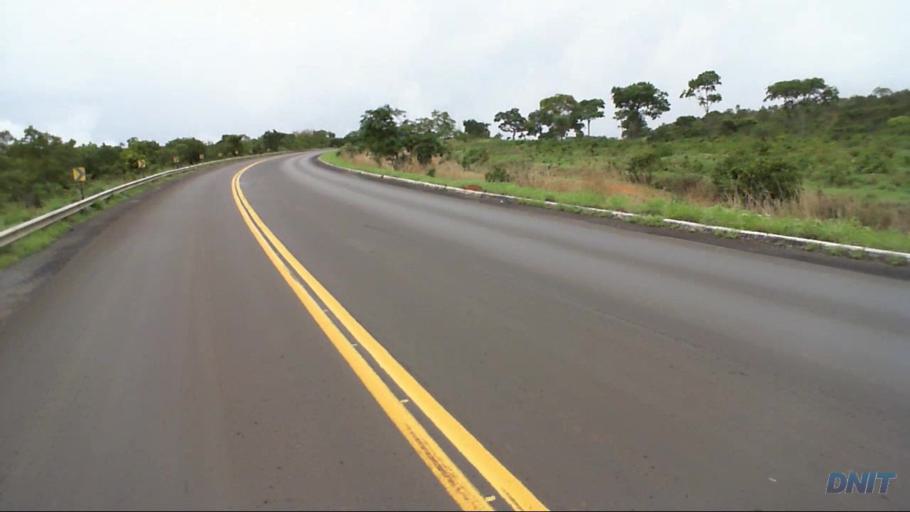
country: BR
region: Goias
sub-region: Padre Bernardo
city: Padre Bernardo
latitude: -15.1933
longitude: -48.4385
